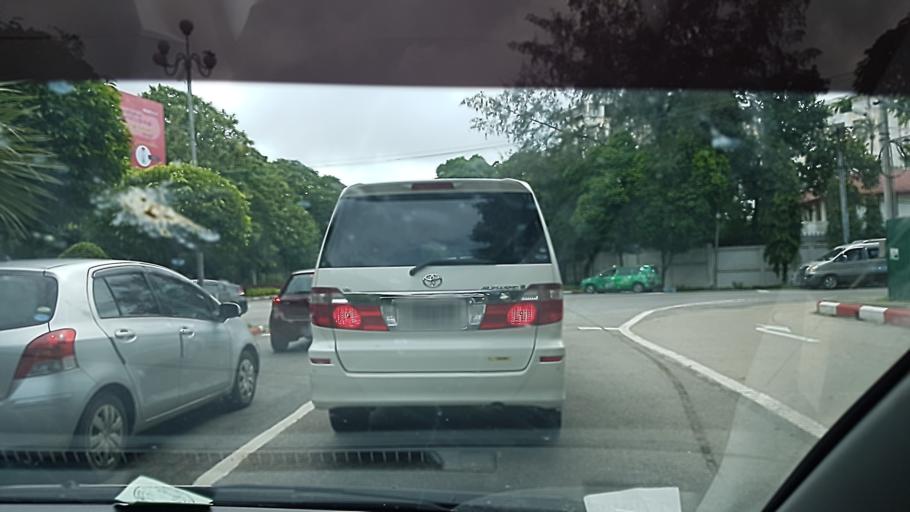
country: MM
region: Yangon
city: Yangon
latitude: 16.7941
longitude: 96.1446
